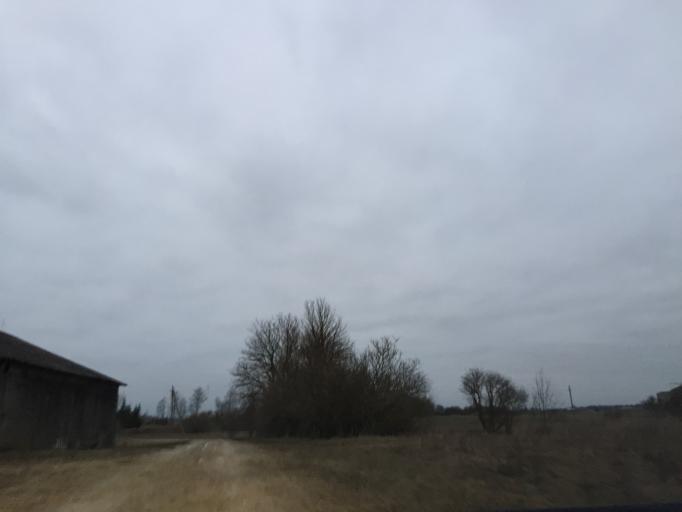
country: LT
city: Zagare
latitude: 56.3389
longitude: 23.2685
